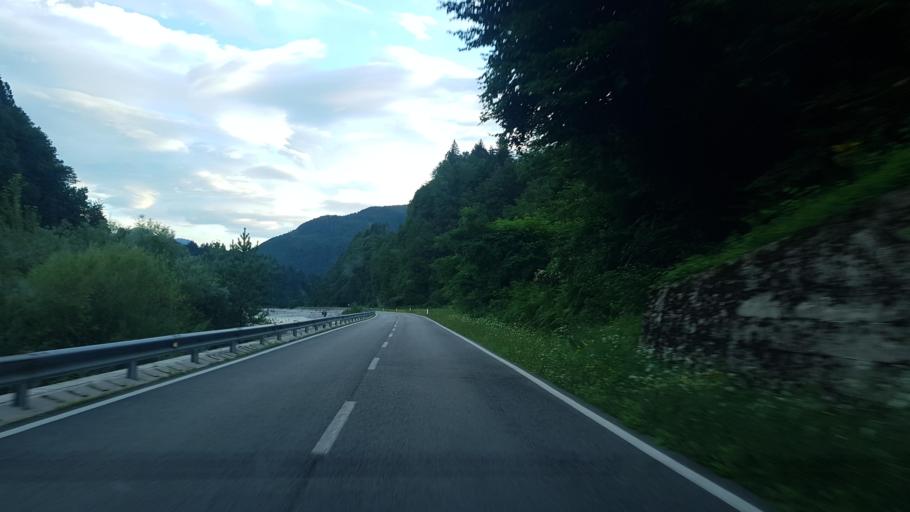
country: IT
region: Friuli Venezia Giulia
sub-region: Provincia di Udine
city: Zuglio
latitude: 46.4649
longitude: 13.0497
